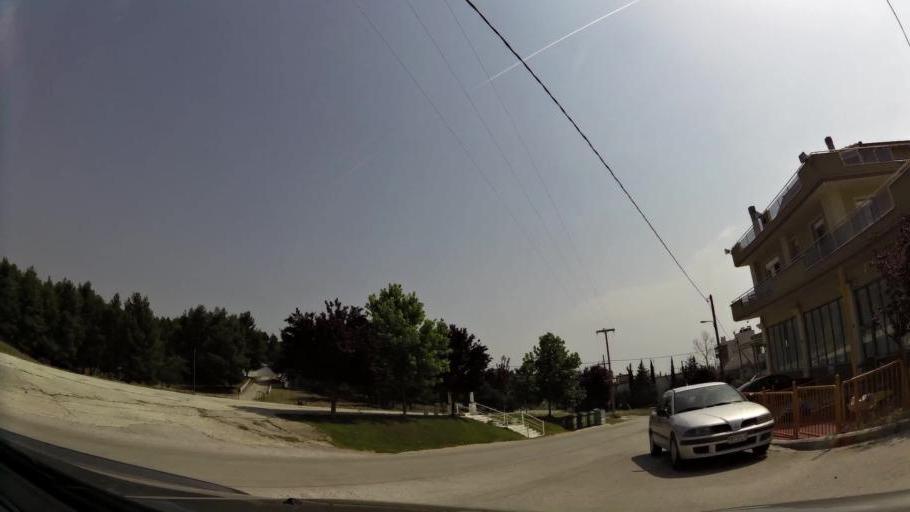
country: GR
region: Central Macedonia
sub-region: Nomos Thessalonikis
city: Efkarpia
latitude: 40.6908
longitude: 22.9566
